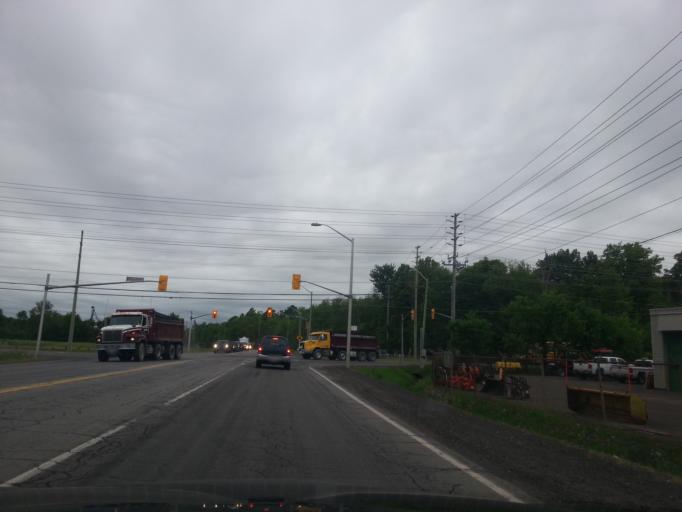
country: CA
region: Ontario
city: Bells Corners
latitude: 45.2698
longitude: -75.8021
